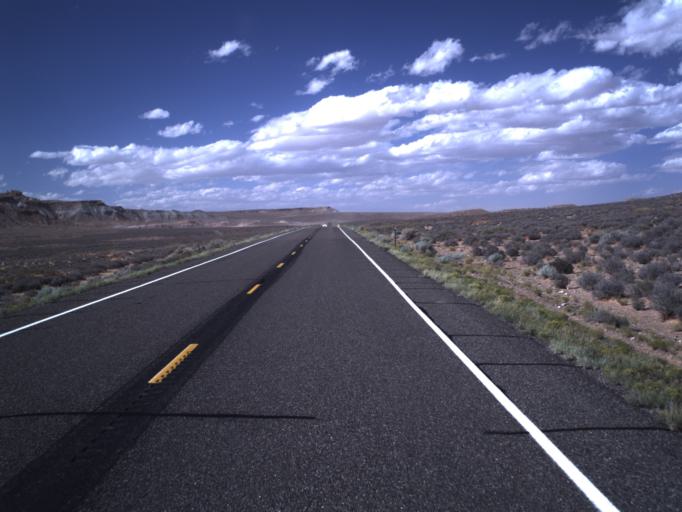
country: US
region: Utah
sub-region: Wayne County
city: Loa
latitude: 38.0849
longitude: -110.6147
